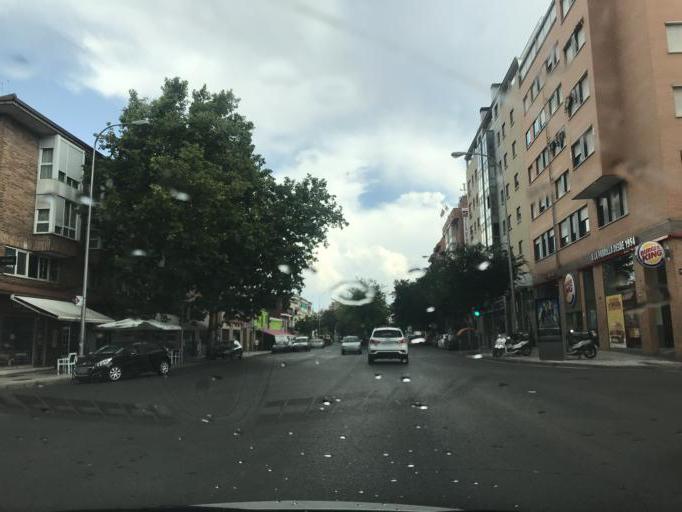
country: ES
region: Madrid
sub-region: Provincia de Madrid
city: Barajas de Madrid
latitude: 40.4738
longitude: -3.5822
